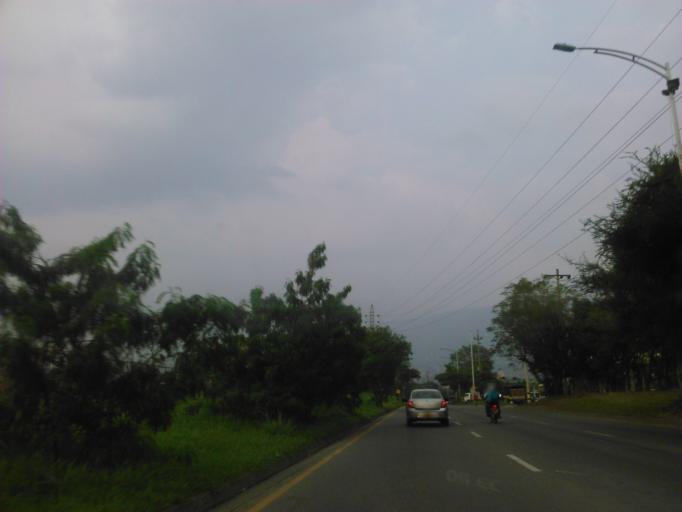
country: CO
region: Antioquia
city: Sabaneta
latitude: 6.1606
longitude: -75.6107
